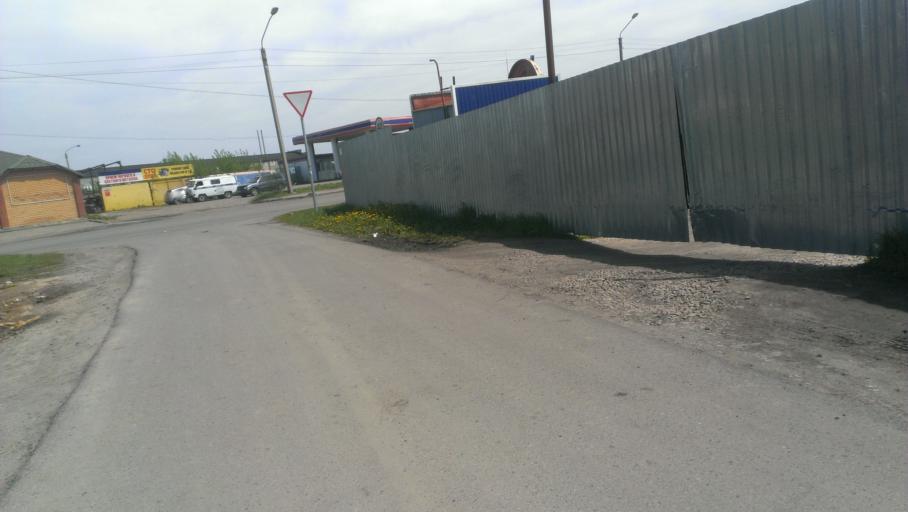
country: RU
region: Altai Krai
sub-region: Gorod Barnaulskiy
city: Barnaul
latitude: 53.3801
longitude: 83.6914
